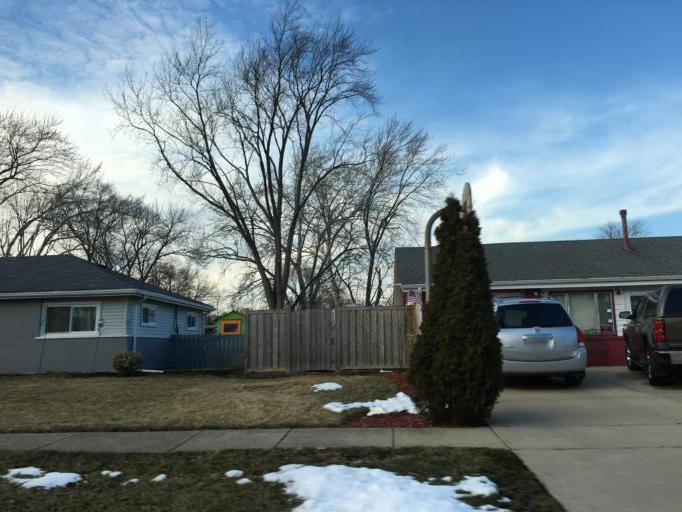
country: US
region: Illinois
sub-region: Cook County
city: Schaumburg
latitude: 42.0354
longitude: -88.0840
